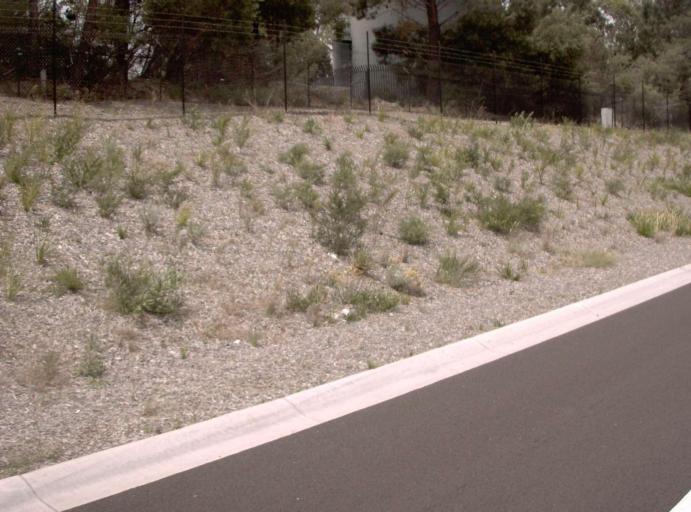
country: AU
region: Victoria
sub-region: Frankston
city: Frankston North
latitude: -38.1334
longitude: 145.1737
